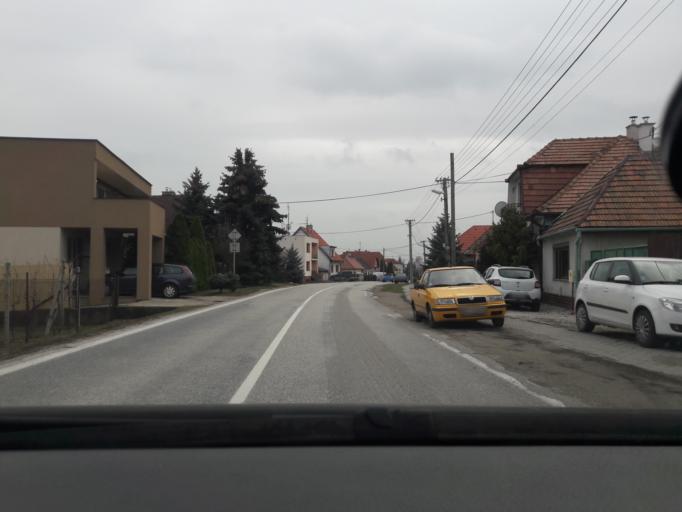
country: SK
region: Trnavsky
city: Smolenice
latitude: 48.4138
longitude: 17.3810
